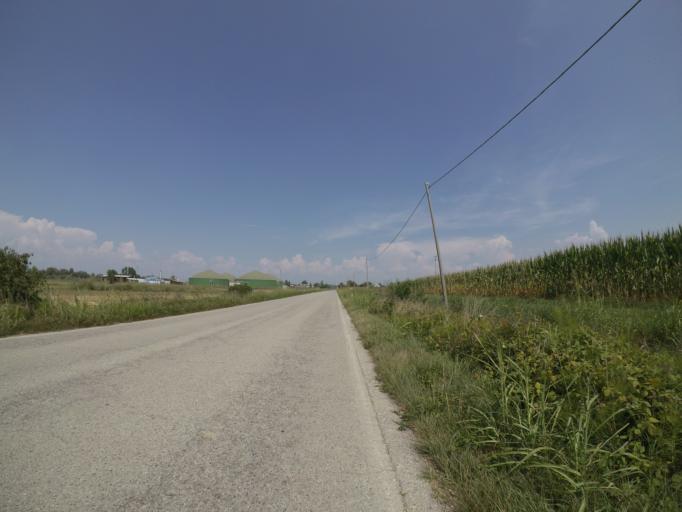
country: IT
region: Friuli Venezia Giulia
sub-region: Provincia di Udine
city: Pocenia
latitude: 45.8585
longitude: 13.1066
